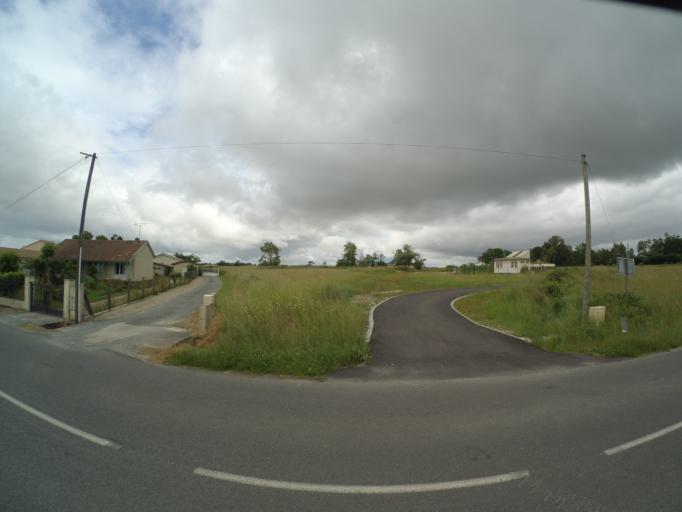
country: FR
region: Aquitaine
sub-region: Departement de la Gironde
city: Lamarque
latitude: 45.0918
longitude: -0.7239
